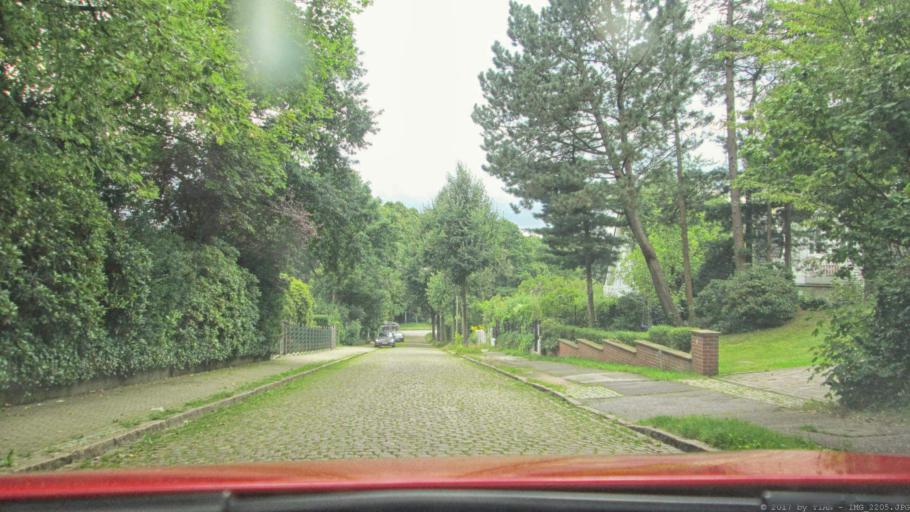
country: DE
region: Schleswig-Holstein
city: Halstenbek
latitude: 53.5667
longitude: 9.8020
